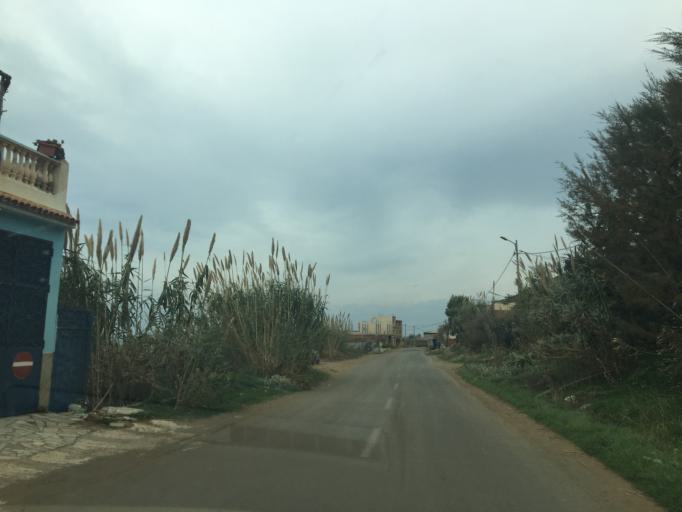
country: DZ
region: Tipaza
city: Tipasa
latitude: 36.6332
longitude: 2.2924
